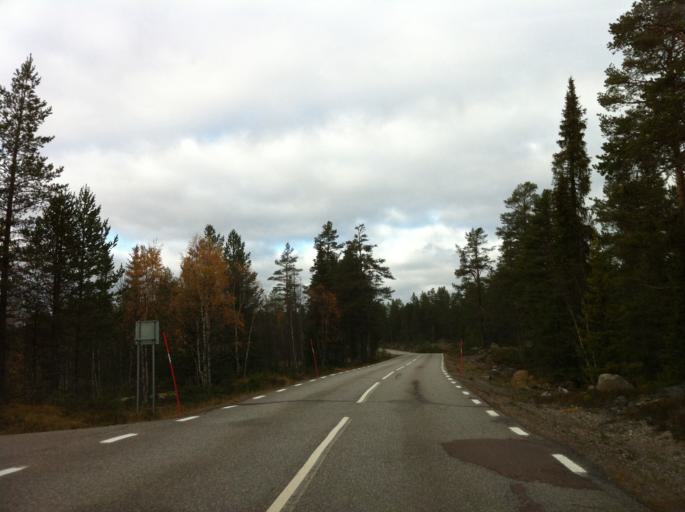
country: NO
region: Hedmark
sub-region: Engerdal
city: Engerdal
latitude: 62.0024
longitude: 12.4225
